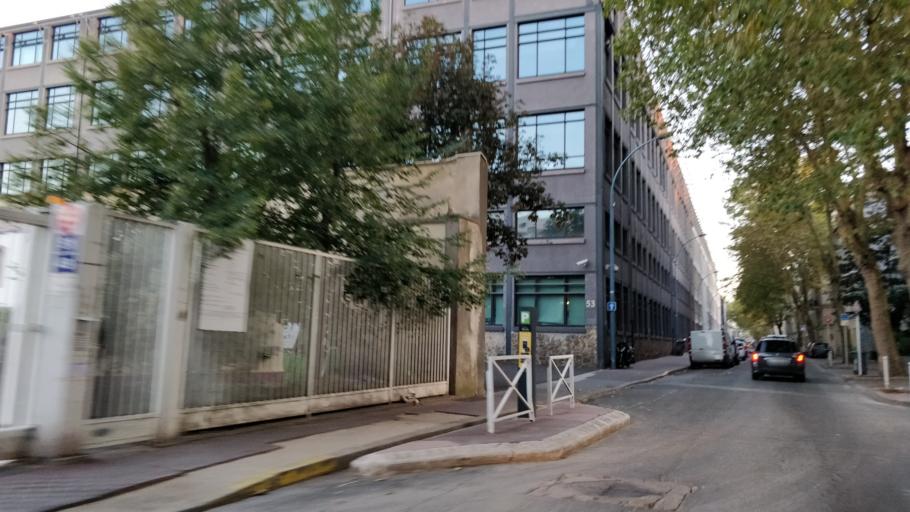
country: FR
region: Ile-de-France
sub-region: Departement des Hauts-de-Seine
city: Montrouge
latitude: 48.8191
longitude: 2.3126
